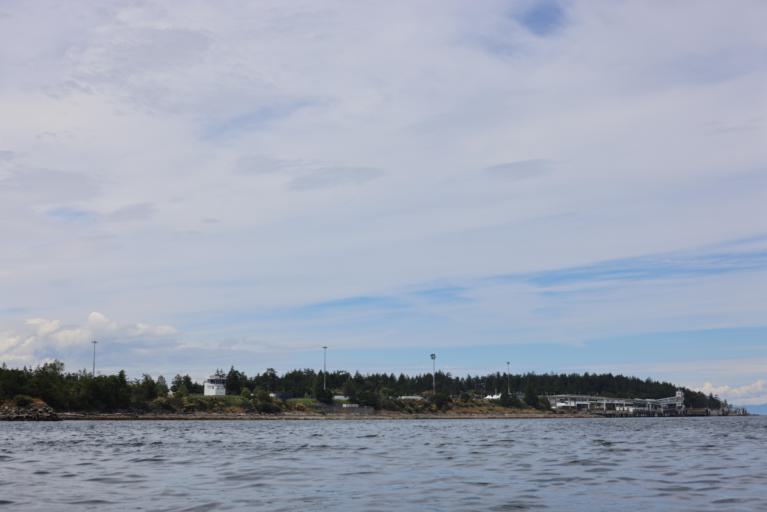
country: CA
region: British Columbia
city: Nanaimo
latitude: 49.1556
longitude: -123.8824
